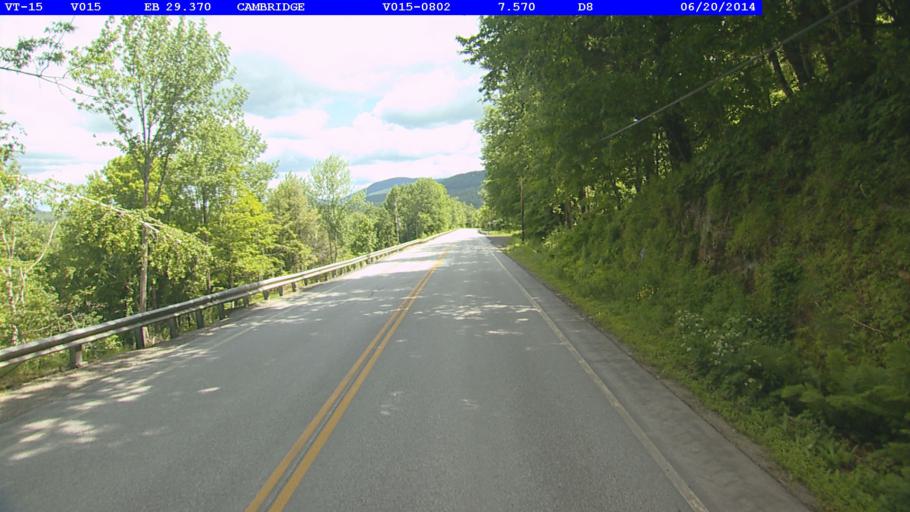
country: US
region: Vermont
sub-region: Lamoille County
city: Johnson
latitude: 44.6638
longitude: -72.7881
